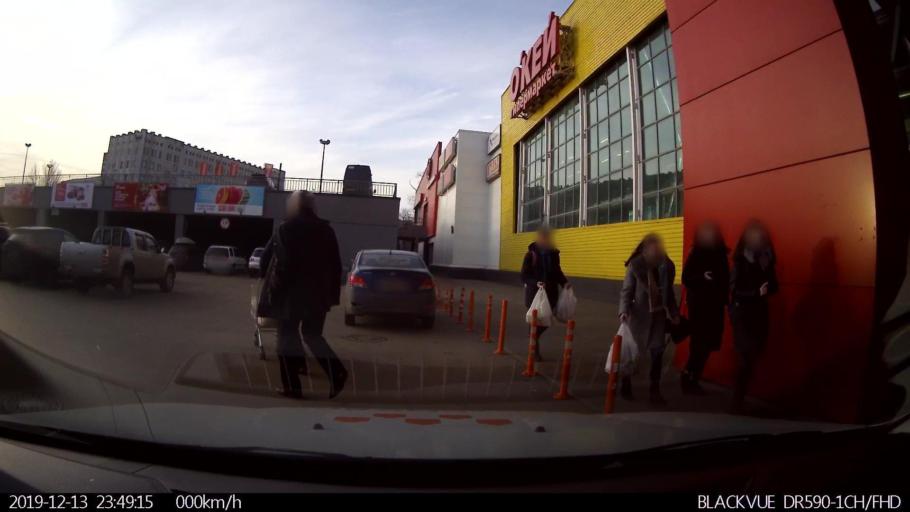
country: RU
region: Nizjnij Novgorod
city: Nizhniy Novgorod
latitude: 56.3007
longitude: 43.9484
